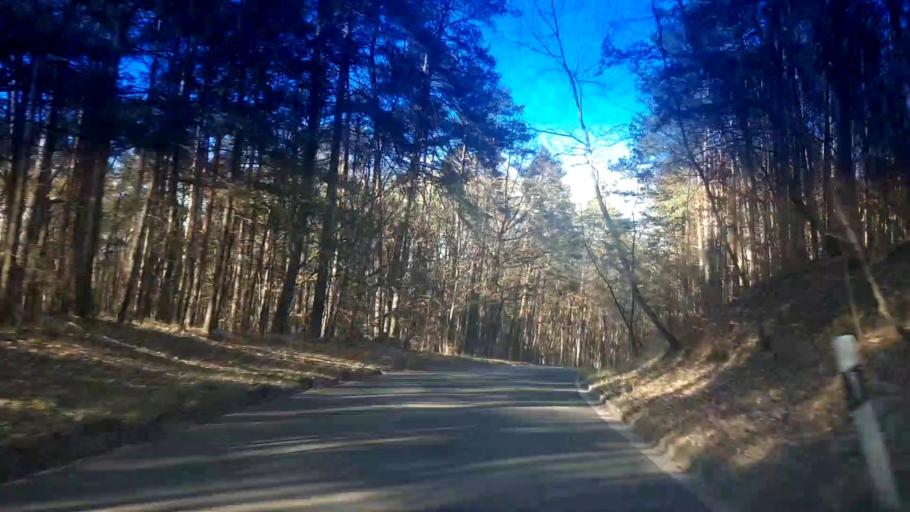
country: DE
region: Bavaria
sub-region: Upper Franconia
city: Lauter
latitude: 49.9614
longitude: 10.7617
